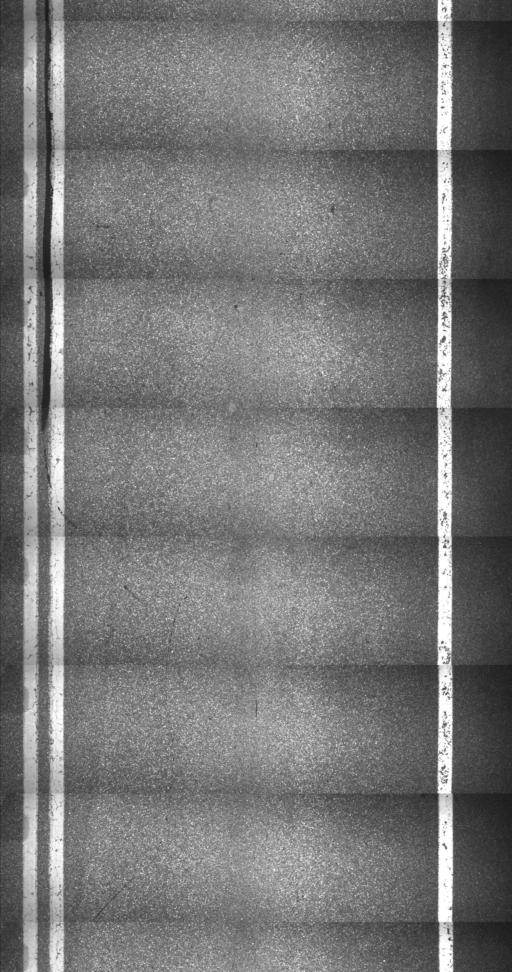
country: US
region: Vermont
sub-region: Addison County
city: Middlebury (village)
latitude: 43.9614
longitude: -73.0243
